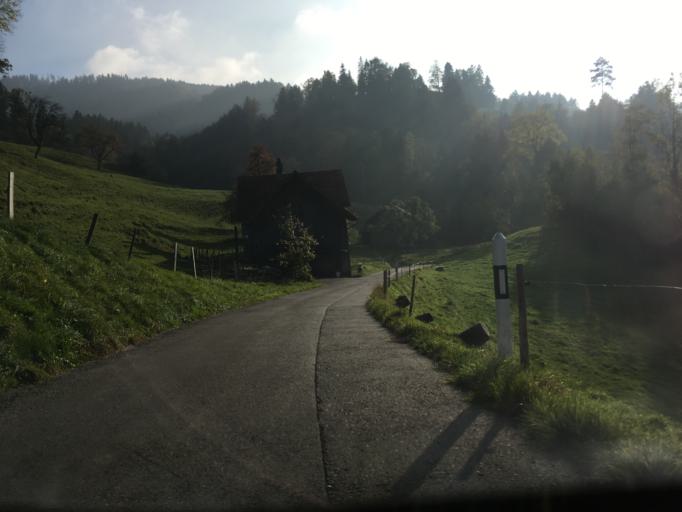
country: CH
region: Saint Gallen
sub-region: Wahlkreis Toggenburg
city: Mosnang
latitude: 47.3308
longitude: 9.0345
